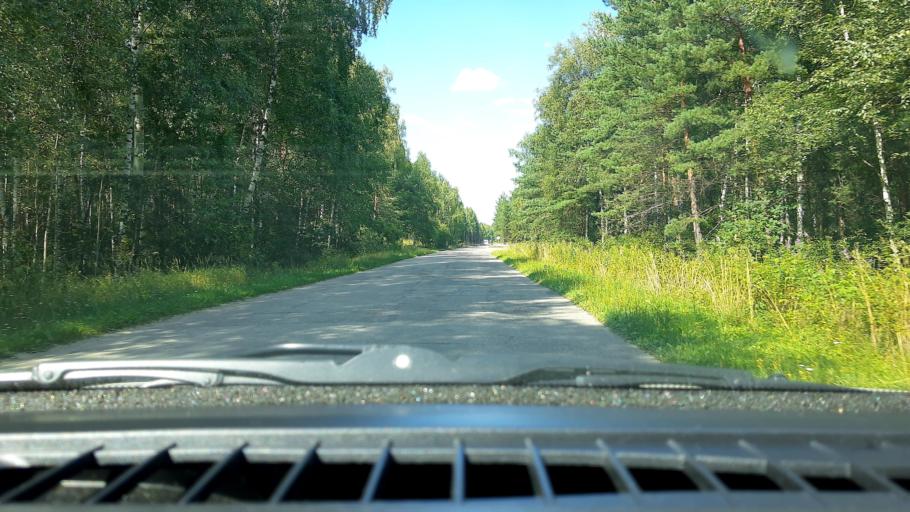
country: RU
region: Nizjnij Novgorod
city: Babino
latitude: 56.3291
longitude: 43.6342
